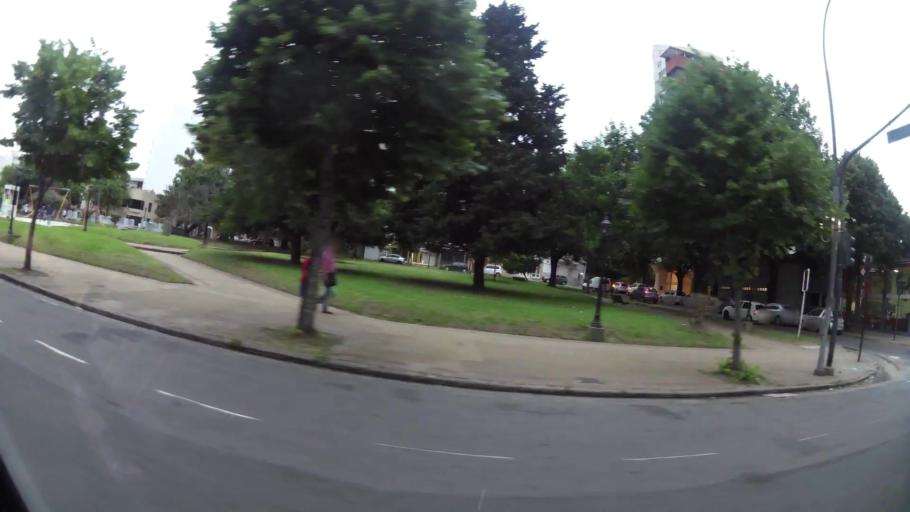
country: AR
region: Buenos Aires
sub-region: Partido de La Plata
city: La Plata
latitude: -34.9059
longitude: -57.9617
